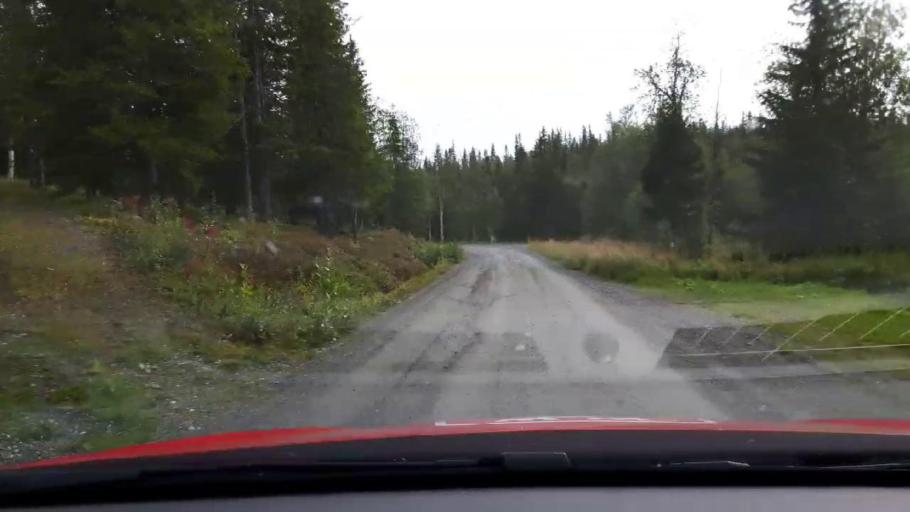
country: SE
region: Jaemtland
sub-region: Are Kommun
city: Are
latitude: 63.7746
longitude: 13.0704
